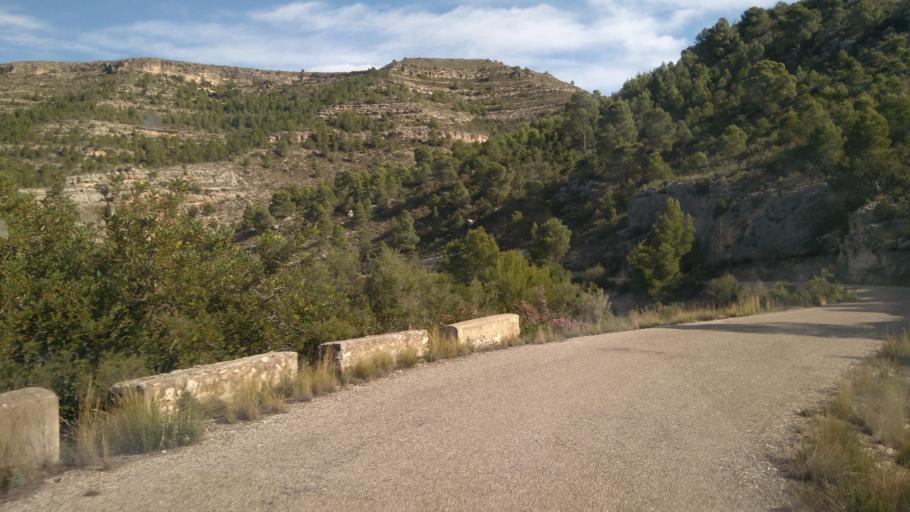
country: ES
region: Valencia
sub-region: Provincia de Valencia
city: Sumacarcer
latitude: 39.1514
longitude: -0.6522
